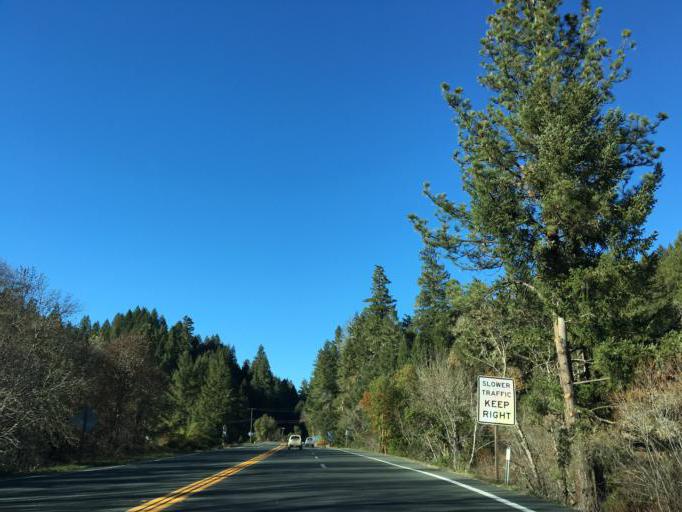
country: US
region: California
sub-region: Mendocino County
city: Brooktrails
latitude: 39.5129
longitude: -123.3877
